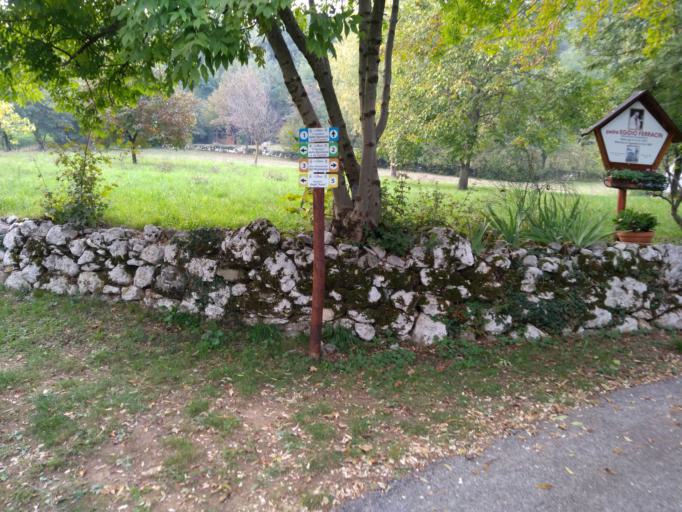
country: IT
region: Veneto
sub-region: Provincia di Vicenza
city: Malo
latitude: 45.6379
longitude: 11.4186
